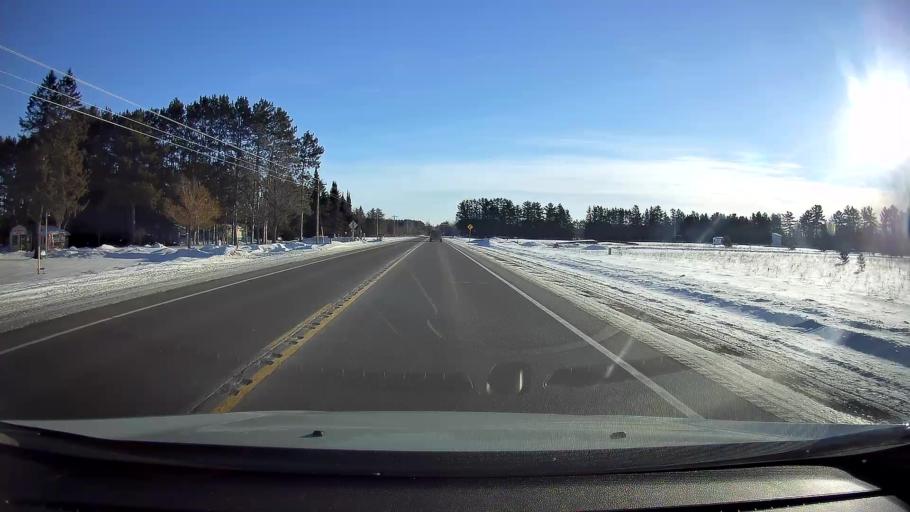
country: US
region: Wisconsin
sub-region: Sawyer County
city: Hayward
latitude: 45.9975
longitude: -91.6054
